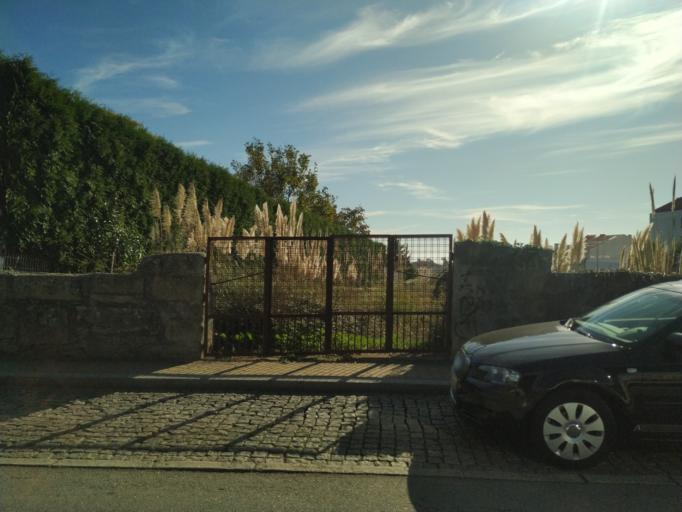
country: PT
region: Porto
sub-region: Vila Nova de Gaia
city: Vilar de Andorinho
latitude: 41.1091
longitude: -8.5966
